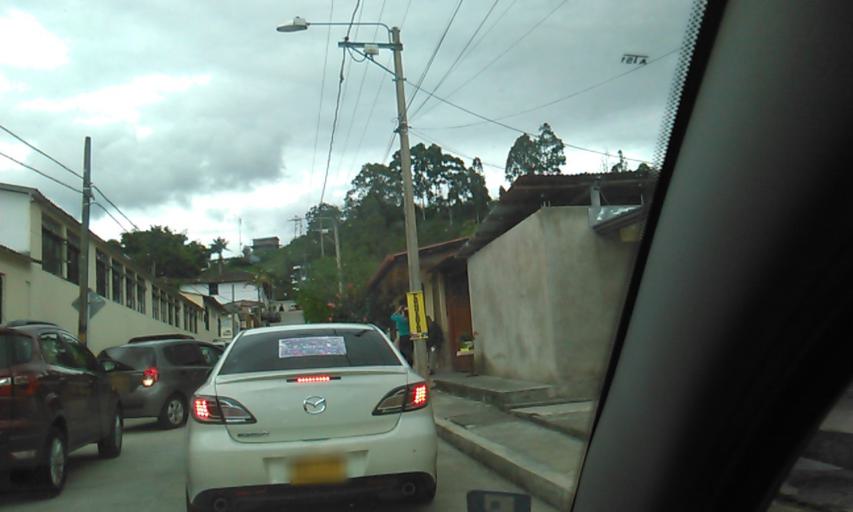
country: CO
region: Quindio
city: Salento
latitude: 4.6388
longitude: -75.5693
